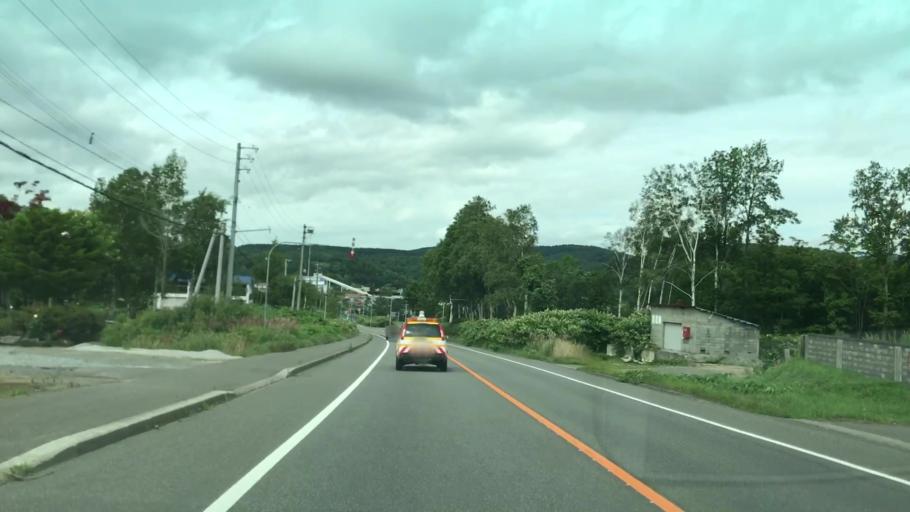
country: JP
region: Hokkaido
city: Niseko Town
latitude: 42.9162
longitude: 140.7485
